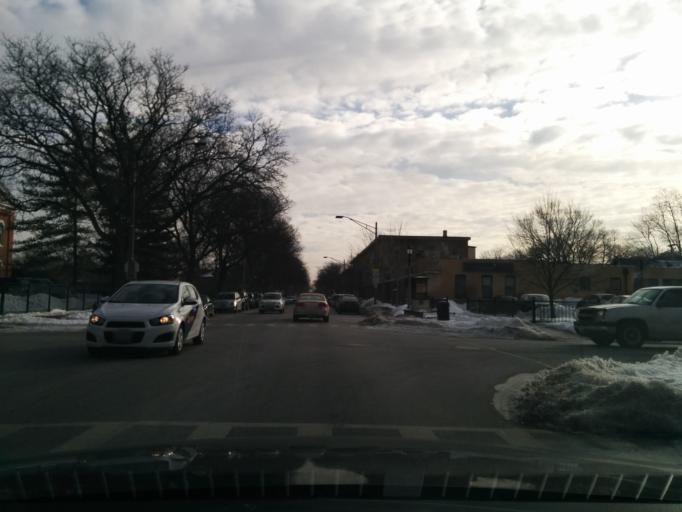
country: US
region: Illinois
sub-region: Cook County
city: Forest Park
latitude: 41.8882
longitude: -87.8200
